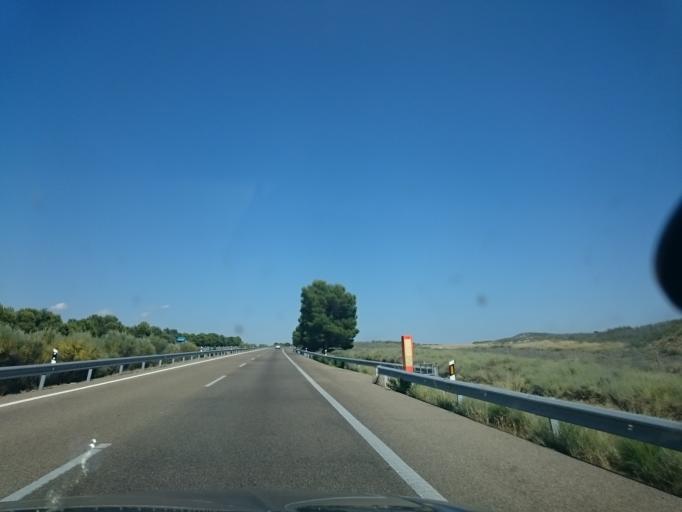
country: ES
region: Aragon
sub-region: Provincia de Huesca
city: Castejon de Monegros
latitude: 41.5187
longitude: -0.2555
